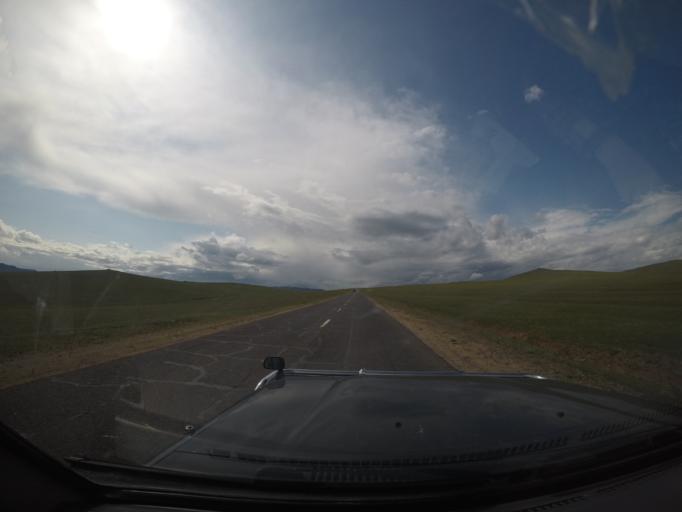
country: MN
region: Hentiy
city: Modot
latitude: 47.6062
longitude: 109.2122
